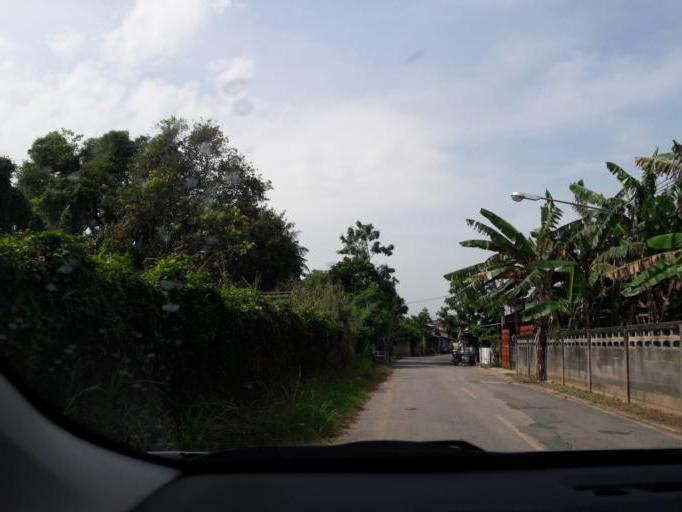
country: TH
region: Ang Thong
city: Ang Thong
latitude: 14.5878
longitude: 100.4636
